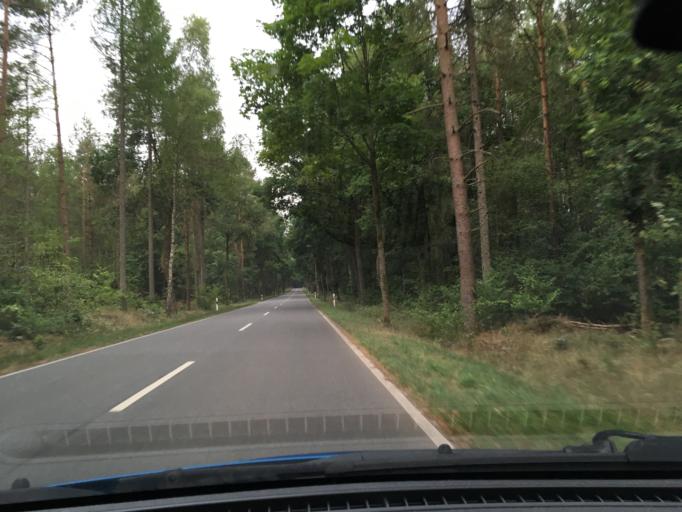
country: DE
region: Lower Saxony
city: Unterluss
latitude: 52.7762
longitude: 10.3039
